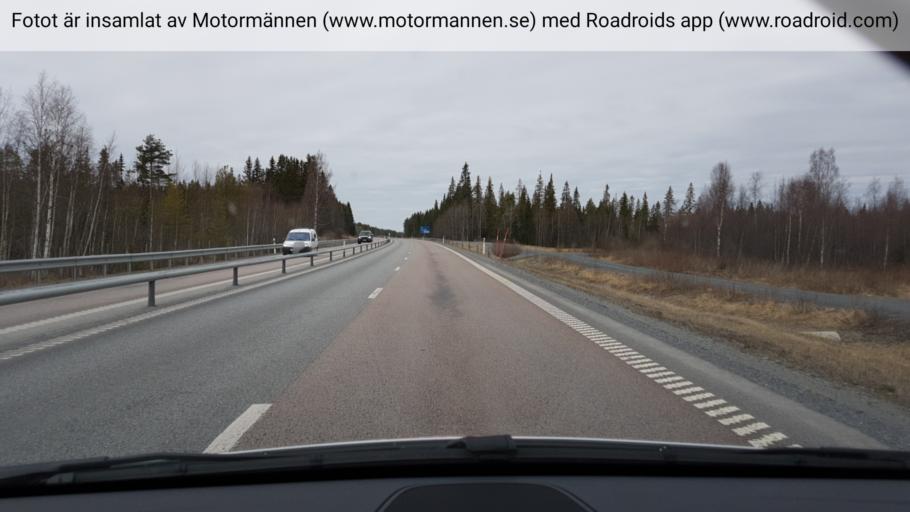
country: SE
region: Jaemtland
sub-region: OEstersunds Kommun
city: Ostersund
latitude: 63.2502
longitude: 14.5863
